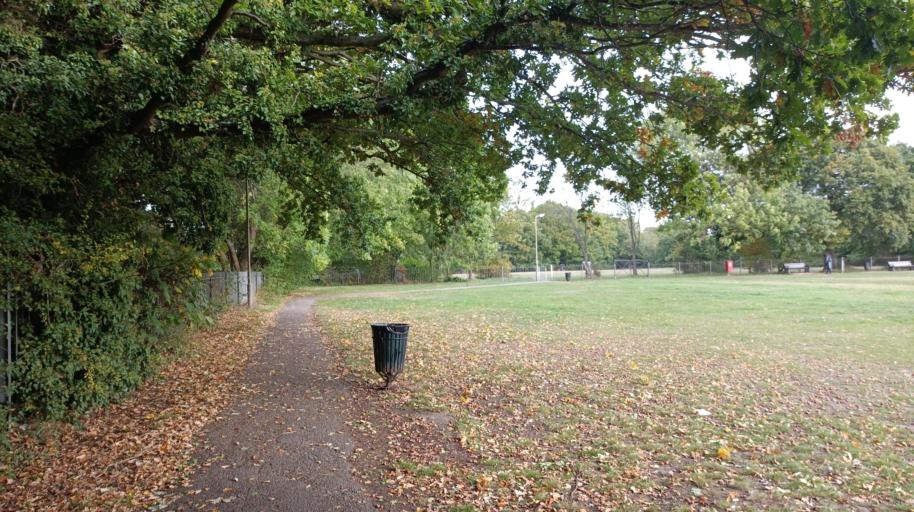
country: GB
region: England
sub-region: Essex
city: South Benfleet
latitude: 51.5632
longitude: 0.5846
